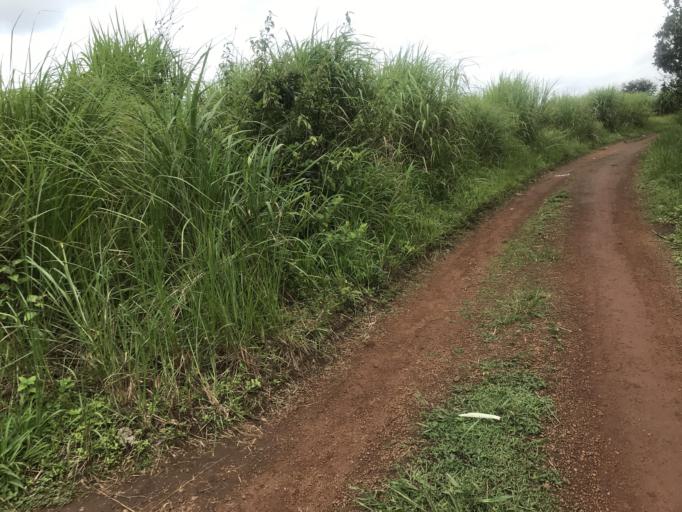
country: SL
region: Eastern Province
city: Buedu
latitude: 8.4658
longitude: -10.3179
